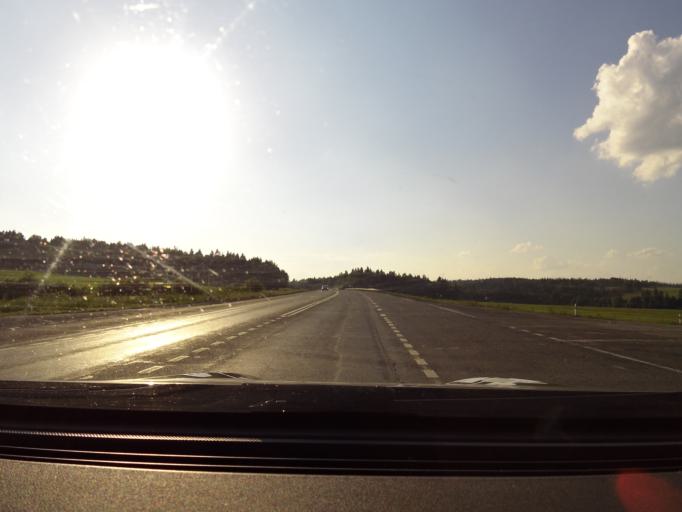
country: RU
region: Sverdlovsk
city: Bilimbay
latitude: 56.8483
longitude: 59.8137
